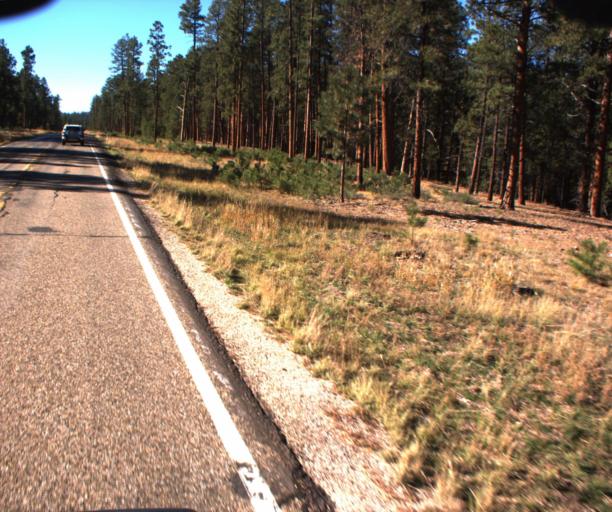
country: US
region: Arizona
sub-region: Coconino County
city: Fredonia
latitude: 36.7273
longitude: -112.1976
